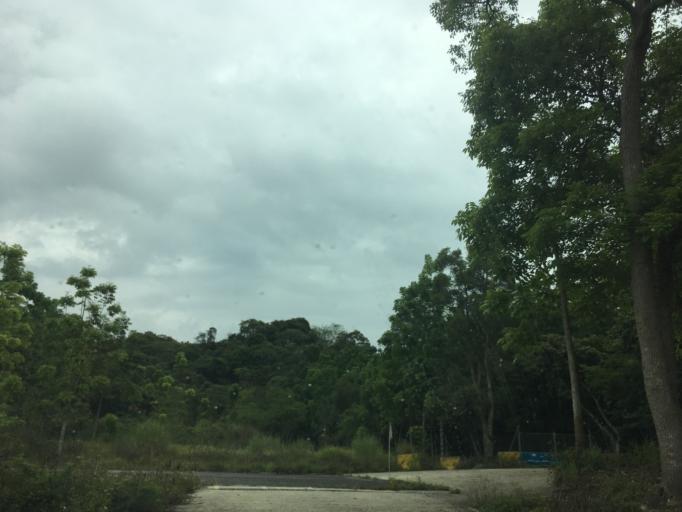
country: TW
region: Taiwan
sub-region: Taichung City
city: Taichung
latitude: 24.0571
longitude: 120.7297
